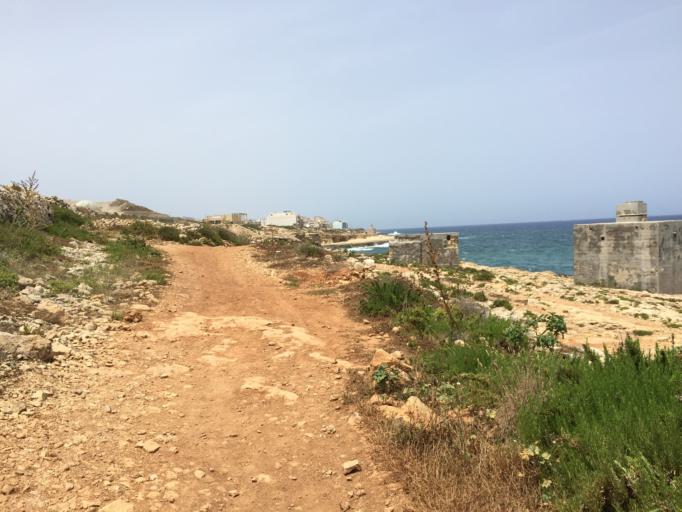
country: MT
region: Ix-Xghajra
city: Xghajra
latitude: 35.8807
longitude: 14.5590
